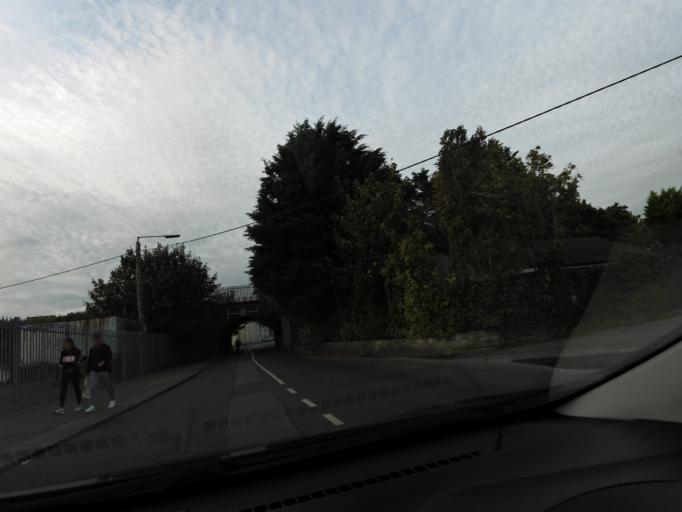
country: IE
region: Leinster
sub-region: An Iarmhi
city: Athlone
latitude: 53.4272
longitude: -7.9436
